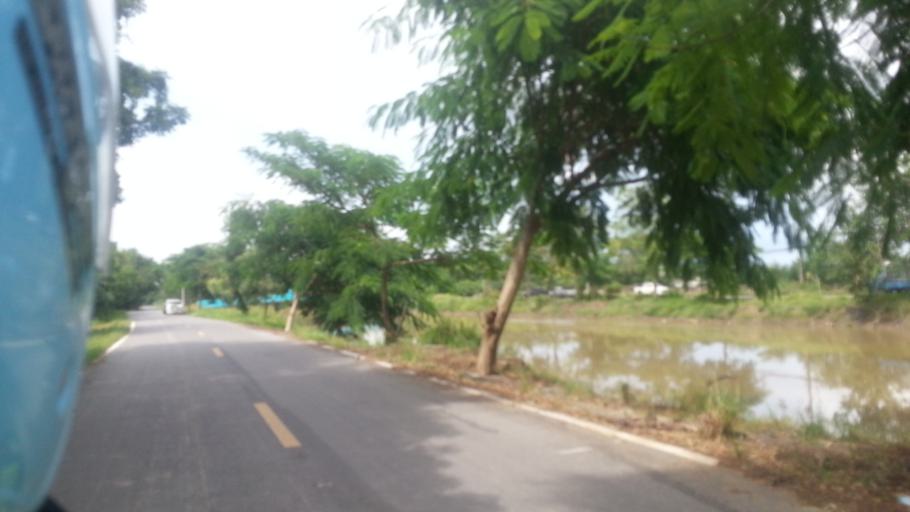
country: TH
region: Pathum Thani
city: Nong Suea
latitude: 14.0714
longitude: 100.8238
